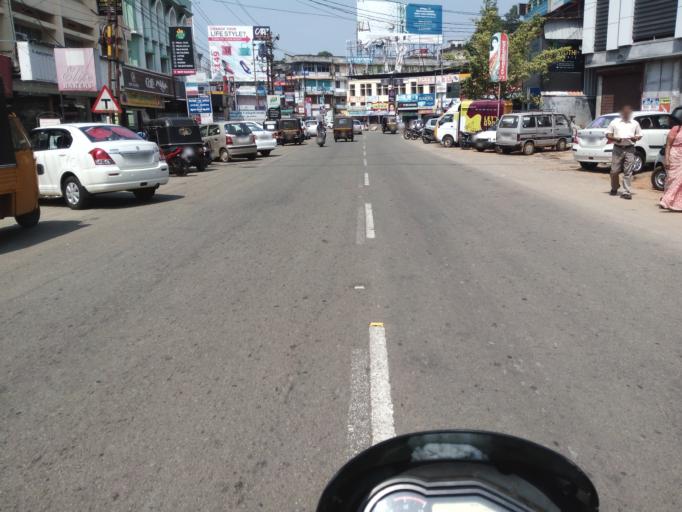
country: IN
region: Kerala
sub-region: Ernakulam
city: Muvattupula
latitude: 9.9002
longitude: 76.7125
